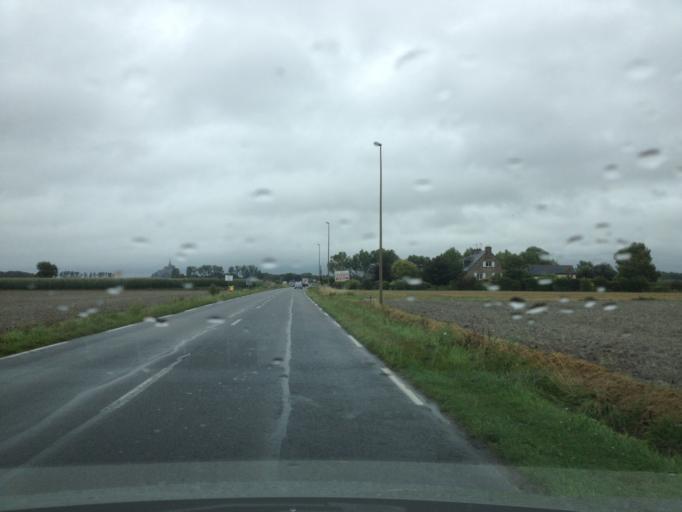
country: FR
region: Lower Normandy
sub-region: Departement de la Manche
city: Pontorson
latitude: 48.6026
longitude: -1.5121
